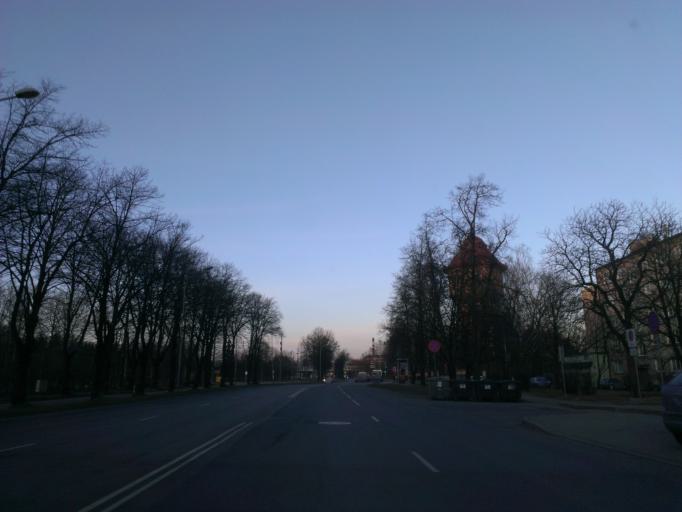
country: LV
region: Riga
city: Jaunciems
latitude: 56.9833
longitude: 24.1533
